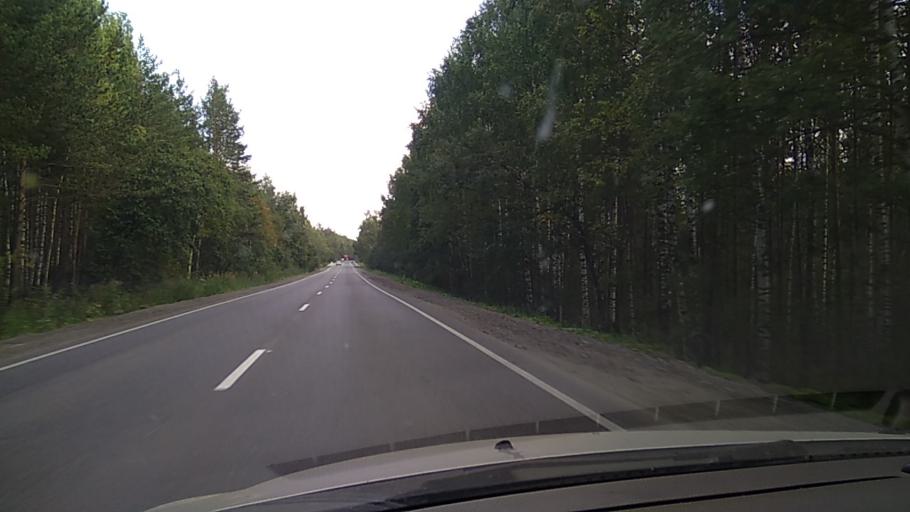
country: RU
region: Chelyabinsk
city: Syrostan
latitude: 55.1235
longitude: 59.7820
